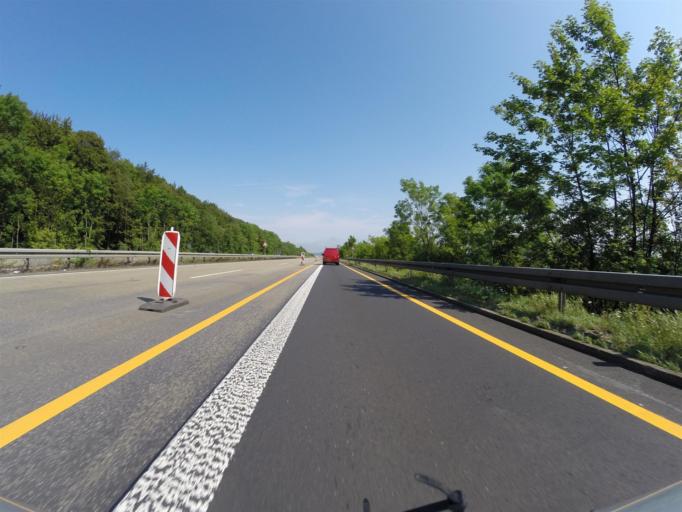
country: DE
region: Hesse
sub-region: Regierungsbezirk Kassel
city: Zierenberg
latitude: 51.3605
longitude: 9.2801
